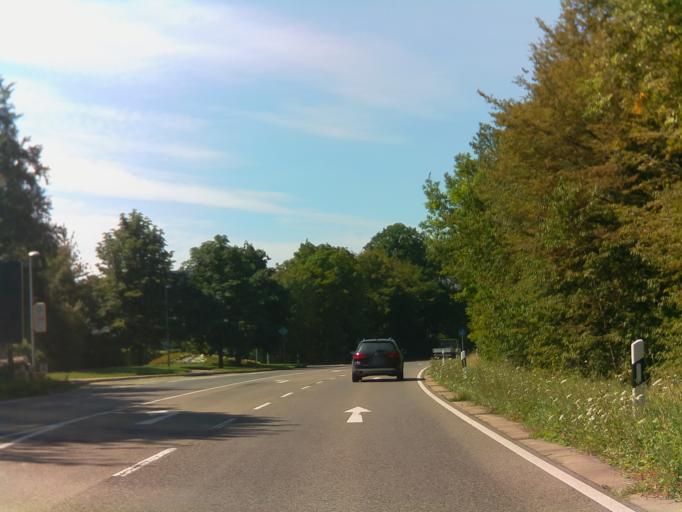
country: DE
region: Baden-Wuerttemberg
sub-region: Regierungsbezirk Stuttgart
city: Gerlingen
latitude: 48.7873
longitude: 9.0556
